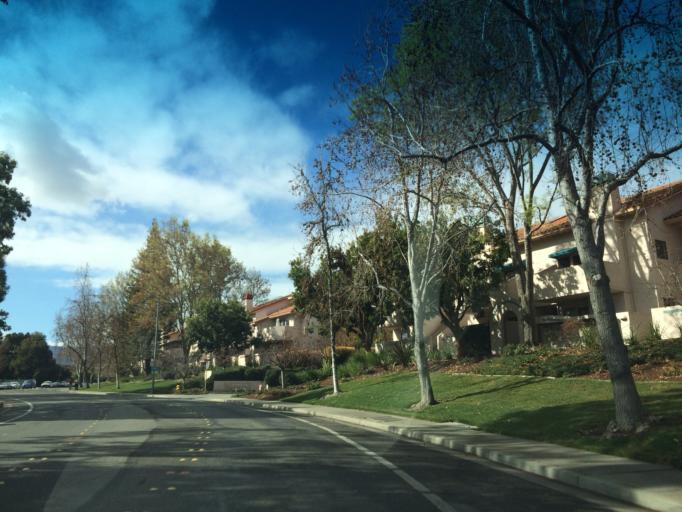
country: US
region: California
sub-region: Santa Clara County
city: Cupertino
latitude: 37.3201
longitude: -122.0258
